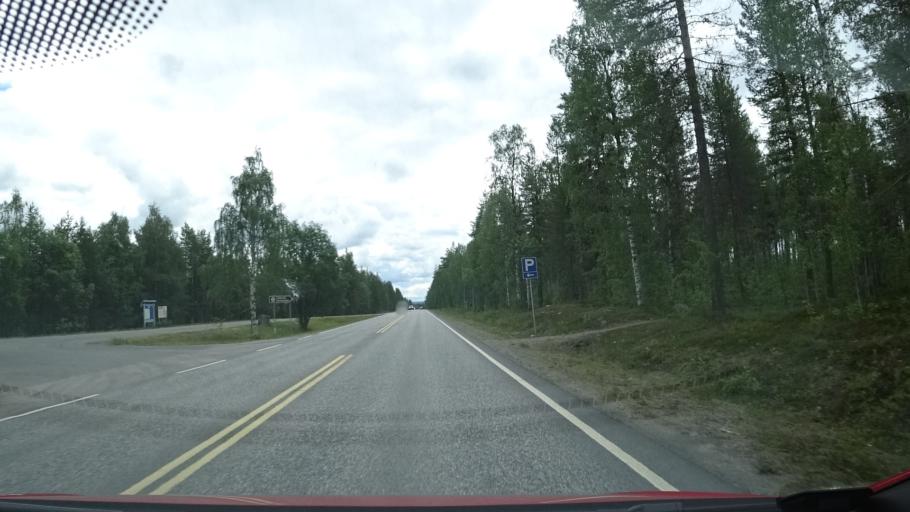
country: FI
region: Lapland
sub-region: Tunturi-Lappi
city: Kittilae
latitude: 67.7412
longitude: 24.8584
